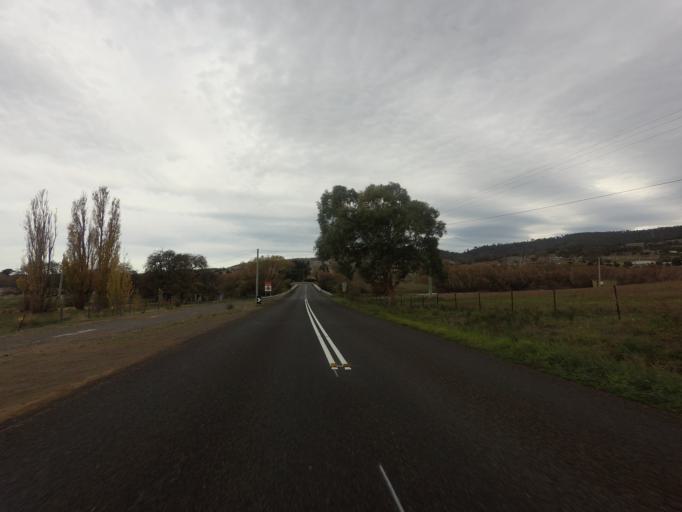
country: AU
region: Tasmania
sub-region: Brighton
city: Bridgewater
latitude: -42.6908
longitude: 147.1938
